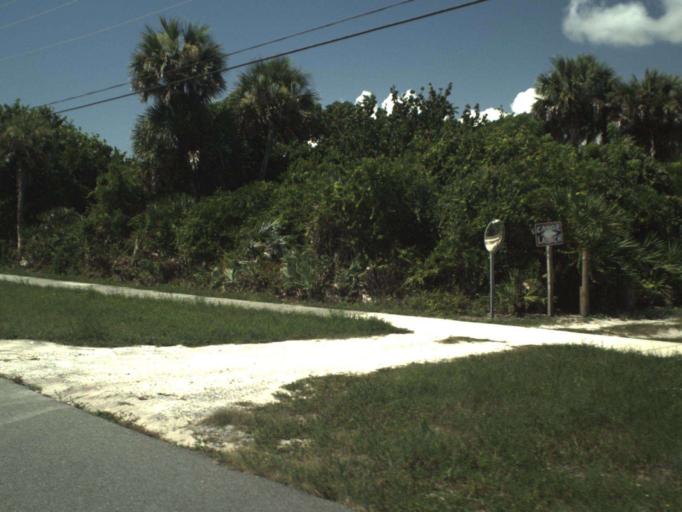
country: US
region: Florida
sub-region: Saint Lucie County
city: Fort Pierce North
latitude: 27.5193
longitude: -80.3101
